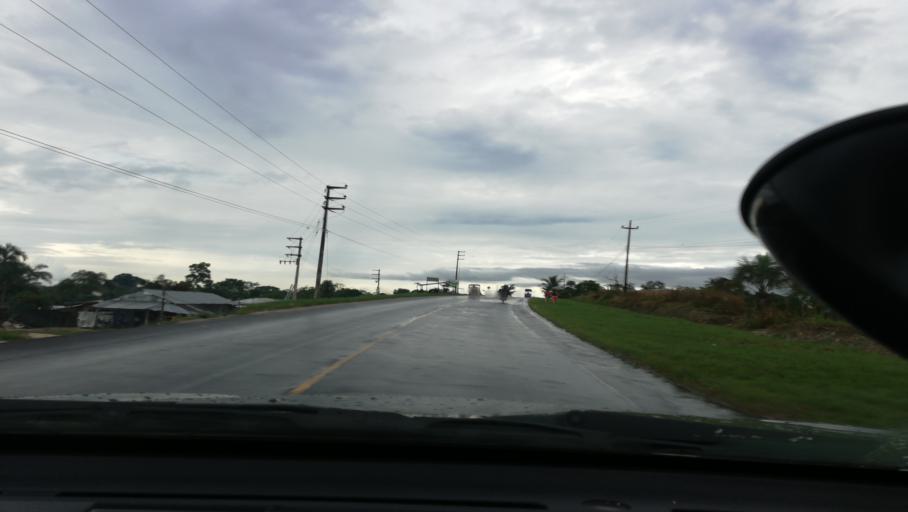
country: PE
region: Loreto
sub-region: Provincia de Maynas
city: Iquitos
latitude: -3.8548
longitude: -73.3377
